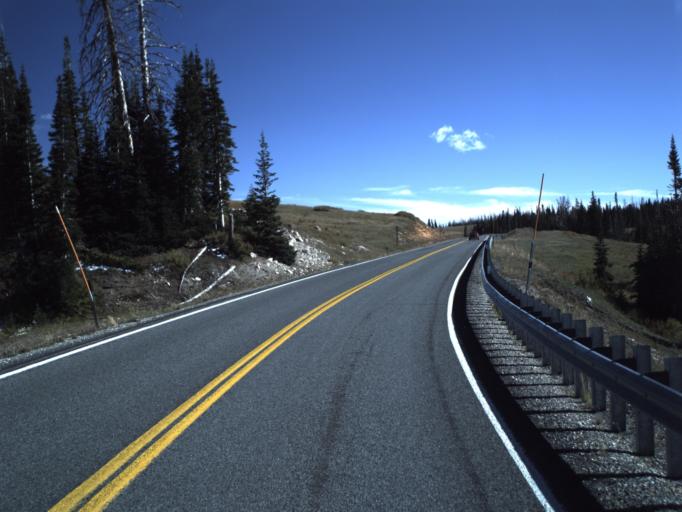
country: US
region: Utah
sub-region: Iron County
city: Parowan
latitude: 37.6754
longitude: -112.8419
